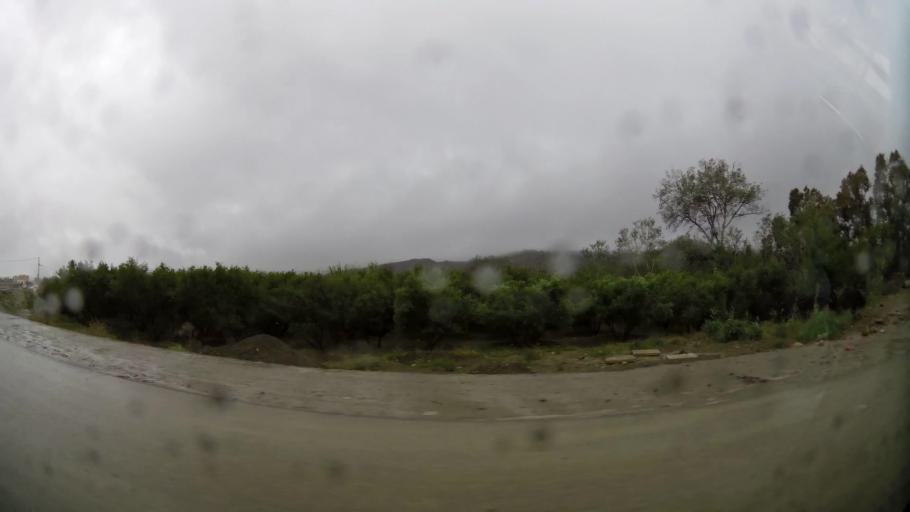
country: MA
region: Taza-Al Hoceima-Taounate
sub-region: Taza
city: Aknoul
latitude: 34.8100
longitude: -3.7359
